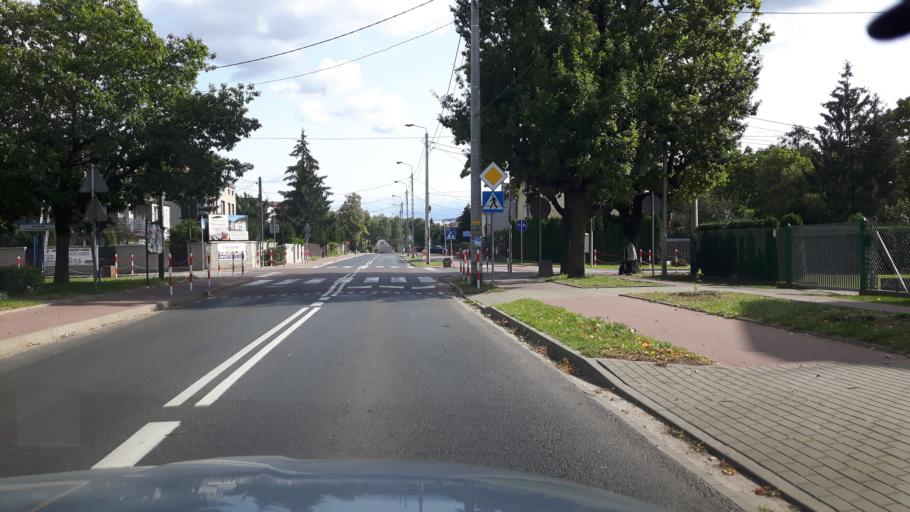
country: PL
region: Masovian Voivodeship
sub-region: Powiat wolominski
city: Wolomin
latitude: 52.3502
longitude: 21.2310
